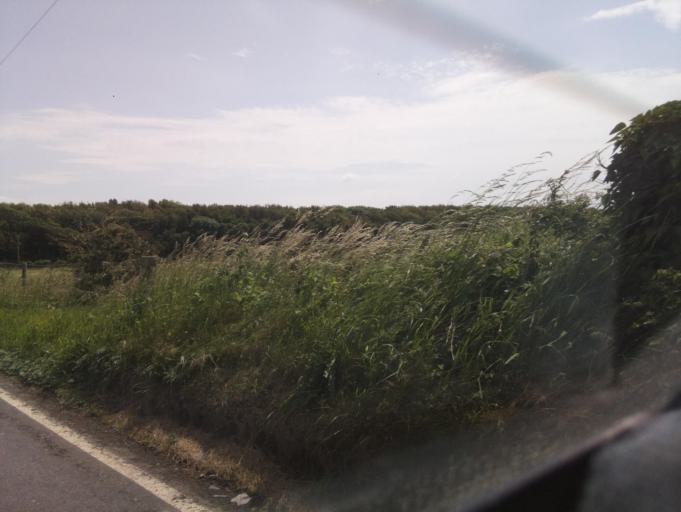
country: GB
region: Wales
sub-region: Vale of Glamorgan
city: Wick
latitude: 51.4522
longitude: -3.5825
